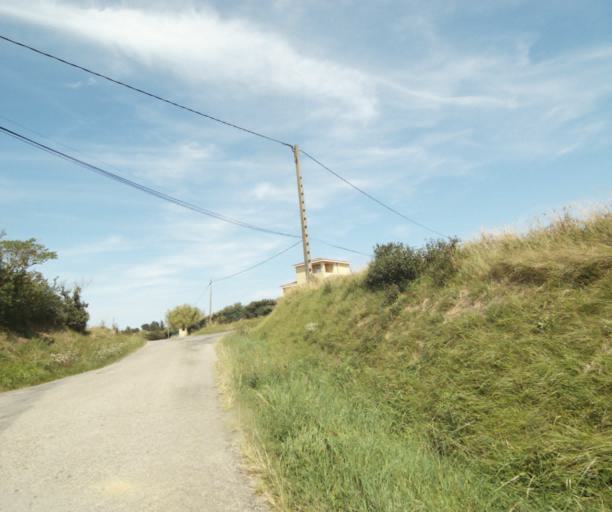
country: FR
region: Midi-Pyrenees
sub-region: Departement de la Haute-Garonne
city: Gaillac-Toulza
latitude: 43.2648
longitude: 1.4100
